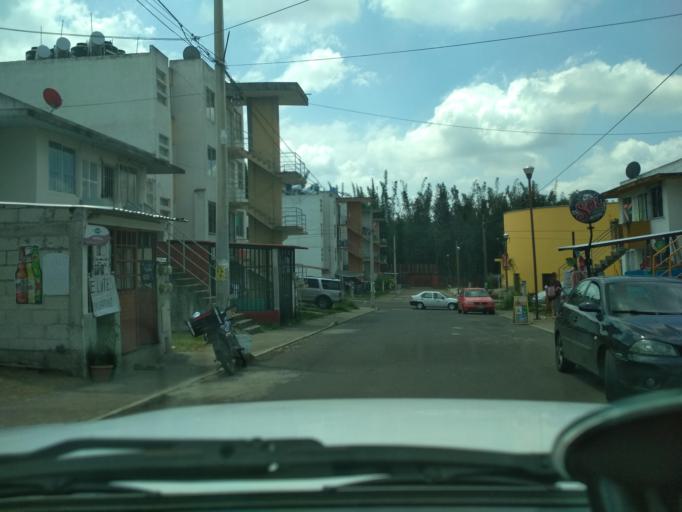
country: MX
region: Veracruz
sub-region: Fortin
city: Fraccionamiento los Alamos
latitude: 18.9304
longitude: -96.9757
